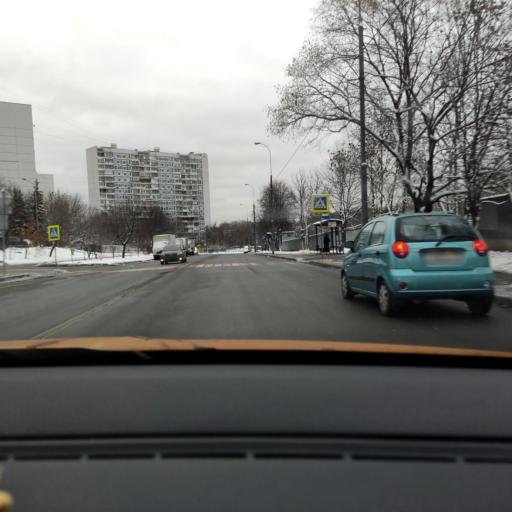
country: RU
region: Moscow
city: Zyablikovo
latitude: 55.6078
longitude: 37.7565
